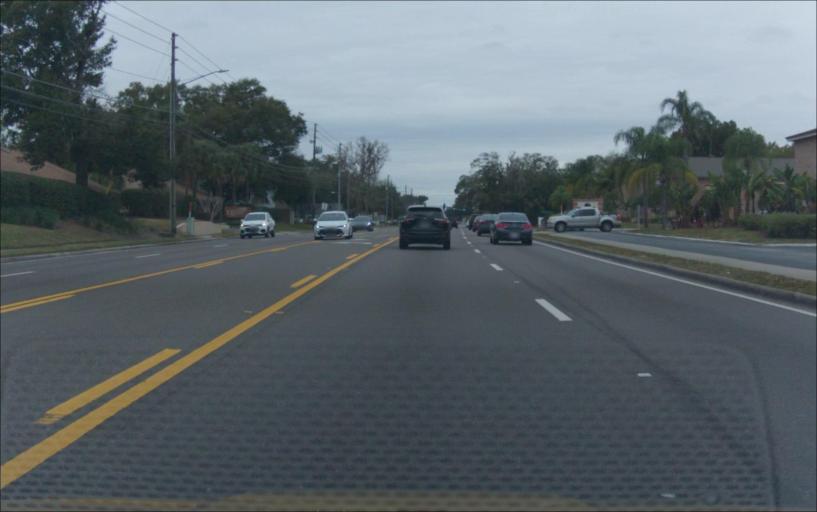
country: US
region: Florida
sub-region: Orange County
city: Winter Park
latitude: 28.6242
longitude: -81.3366
